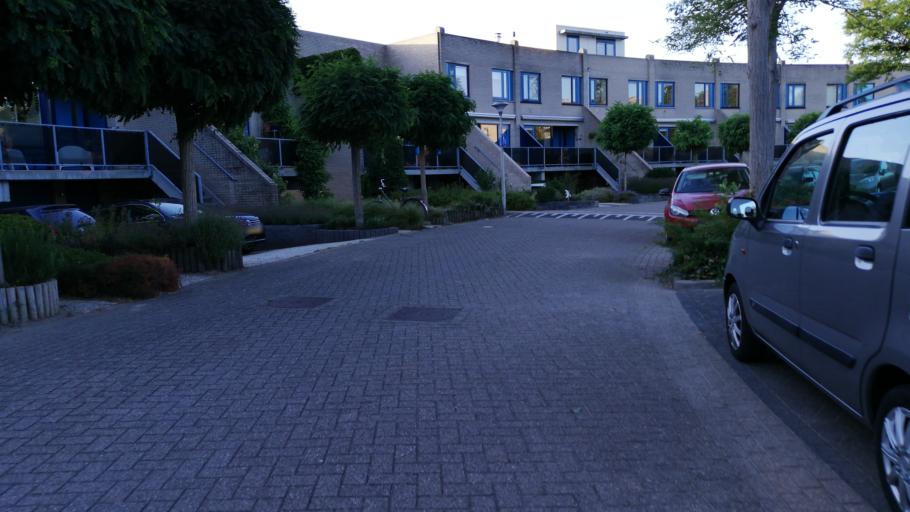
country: NL
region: Overijssel
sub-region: Gemeente Zwolle
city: Zwolle
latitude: 52.4978
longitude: 6.0914
